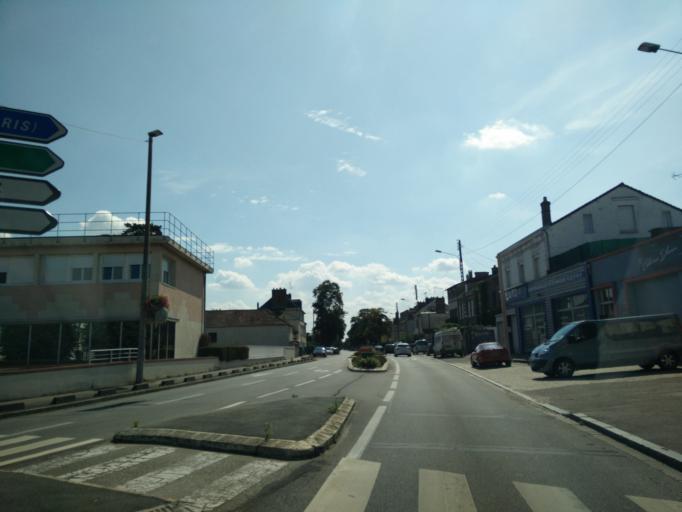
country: FR
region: Haute-Normandie
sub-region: Departement de l'Eure
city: Vernon
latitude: 49.0905
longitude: 1.4898
